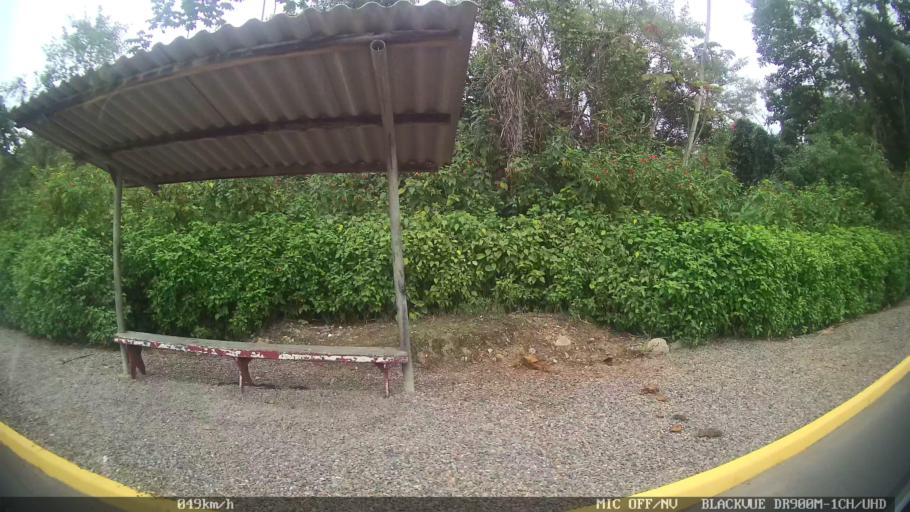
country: BR
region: Santa Catarina
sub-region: Joinville
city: Joinville
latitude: -26.2160
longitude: -48.9139
